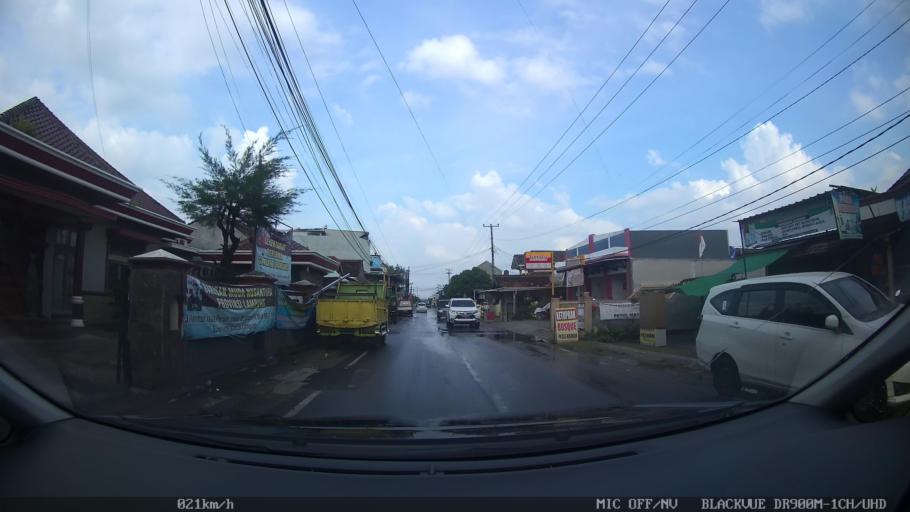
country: ID
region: Lampung
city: Kedaton
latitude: -5.3911
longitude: 105.3011
